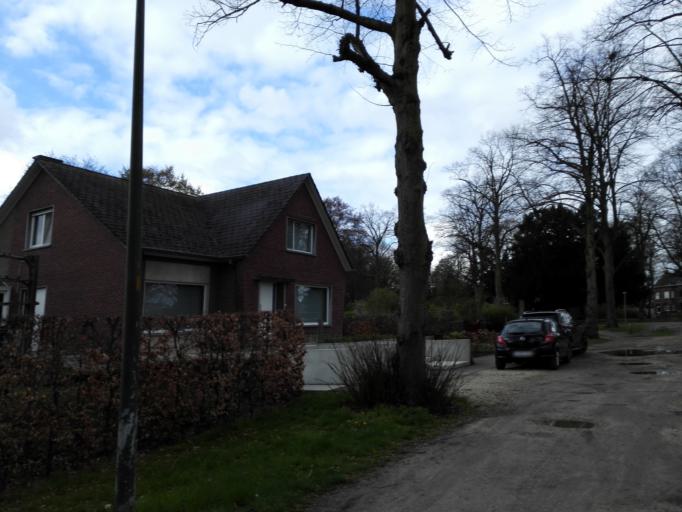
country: BE
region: Flanders
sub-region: Provincie Vlaams-Brabant
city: Rotselaar
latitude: 50.9257
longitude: 4.7039
